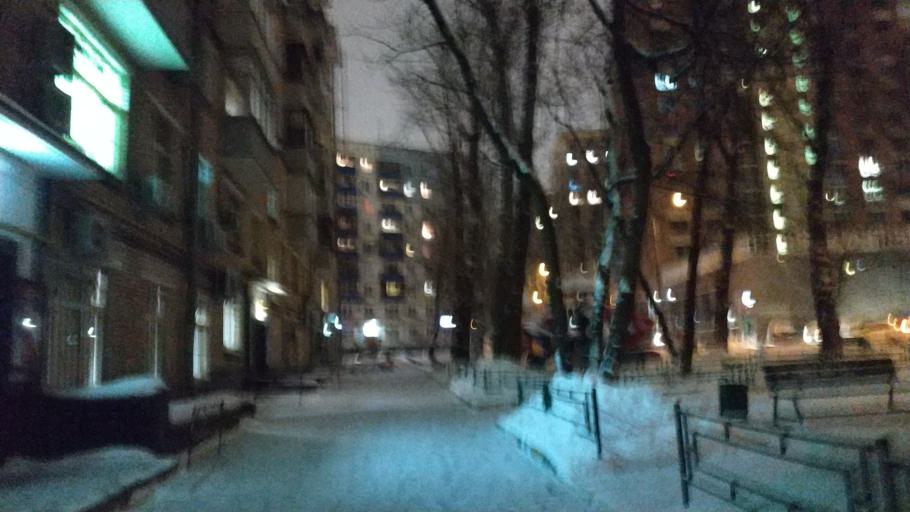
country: RU
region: Moscow
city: Taganskiy
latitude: 55.7306
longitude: 37.6720
